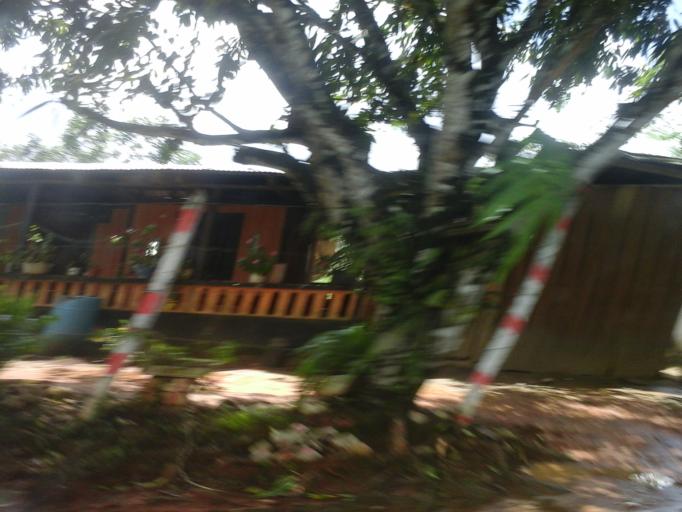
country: CO
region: Caqueta
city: El Doncello
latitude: 1.5974
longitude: -75.0242
